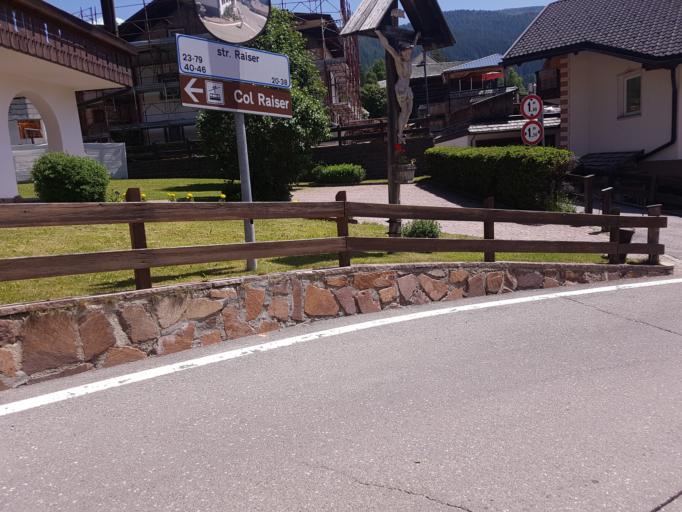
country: IT
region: Trentino-Alto Adige
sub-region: Bolzano
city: Santa Cristina Valgardena
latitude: 46.5617
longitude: 11.7357
